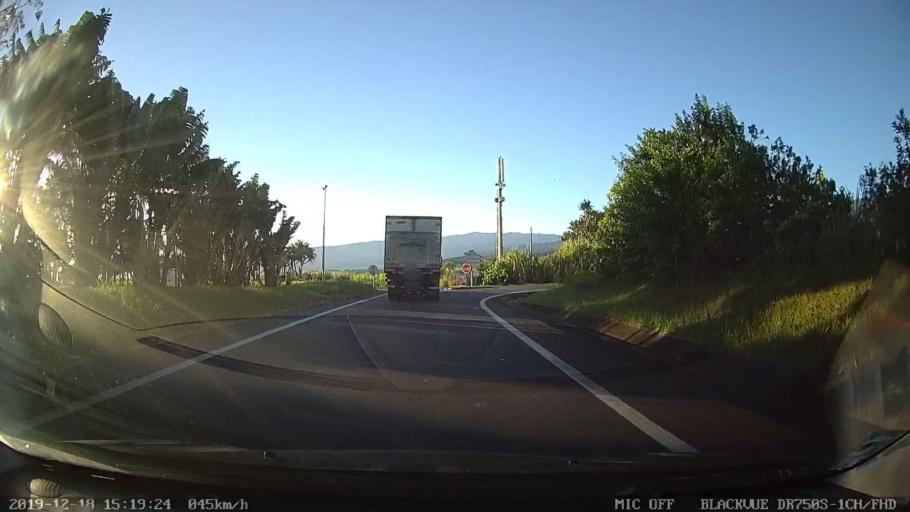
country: RE
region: Reunion
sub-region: Reunion
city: Bras-Panon
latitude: -20.9896
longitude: 55.6611
